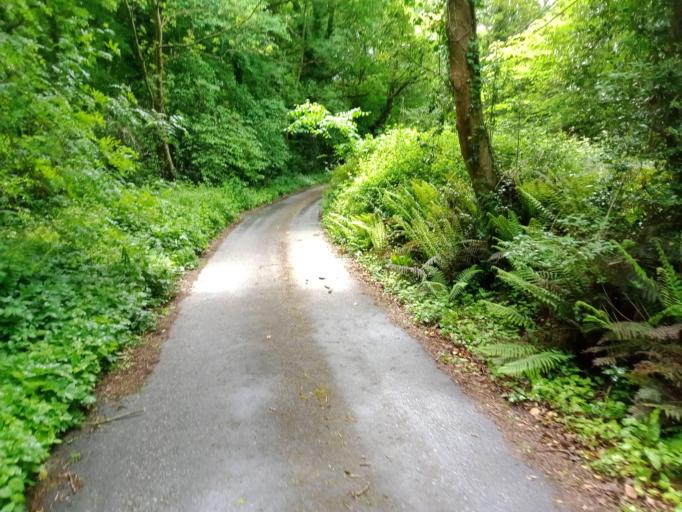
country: IE
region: Leinster
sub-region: Kilkenny
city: Thomastown
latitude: 52.5078
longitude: -7.1303
